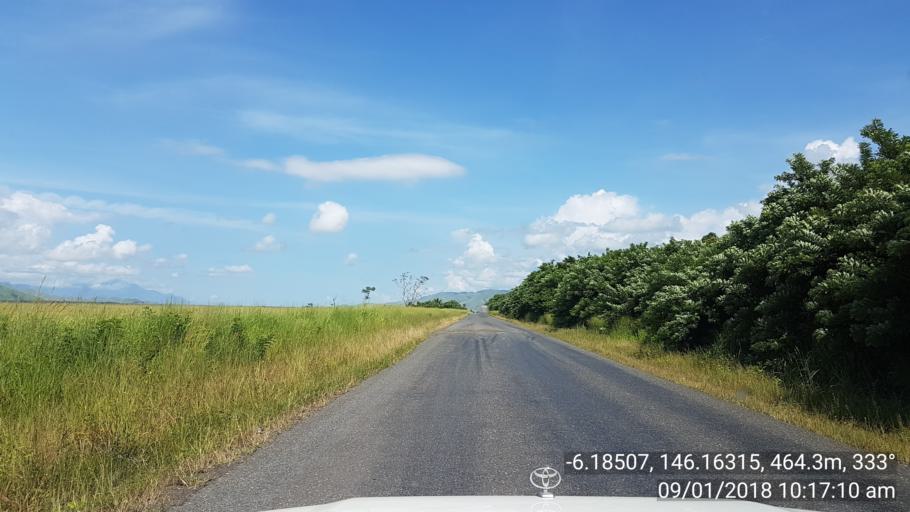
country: PG
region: Eastern Highlands
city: Kainantu
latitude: -6.1846
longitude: 146.1627
